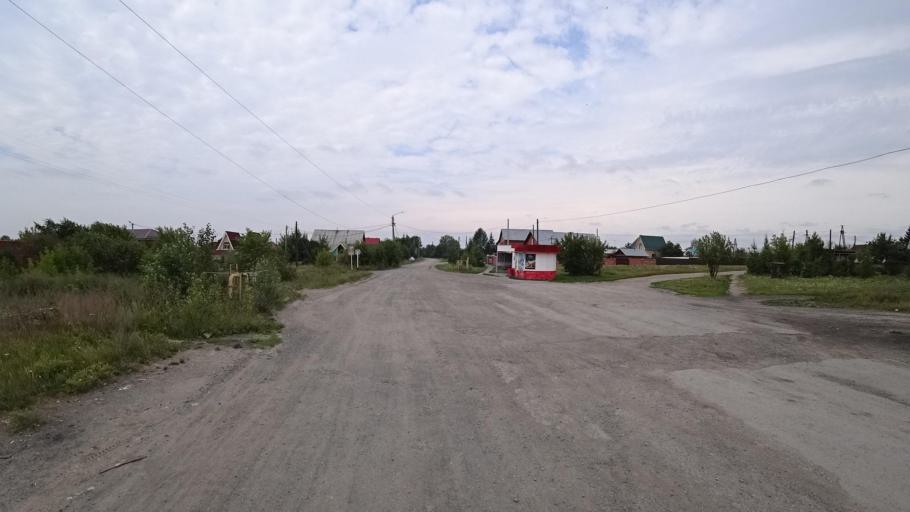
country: RU
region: Sverdlovsk
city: Kamyshlov
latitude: 56.8466
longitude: 62.7419
